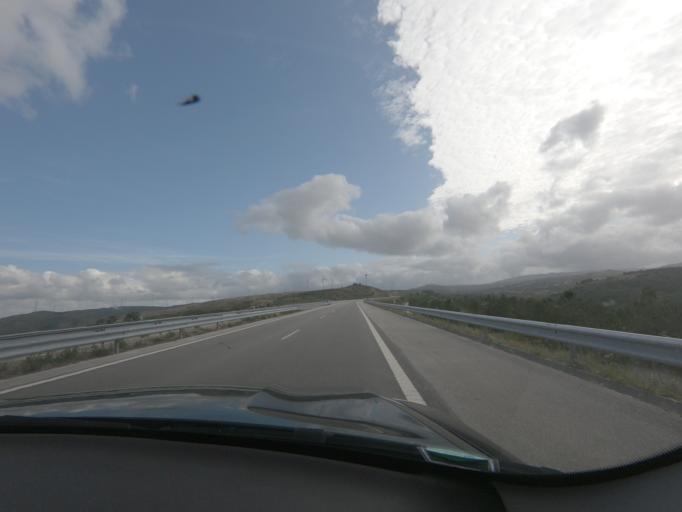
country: PT
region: Viseu
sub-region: Lamego
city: Lamego
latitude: 41.0374
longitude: -7.8612
